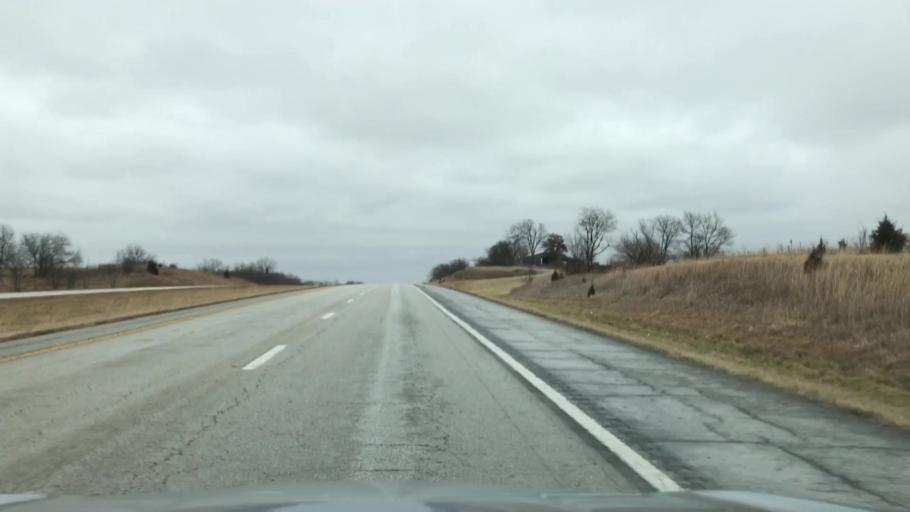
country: US
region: Missouri
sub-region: Caldwell County
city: Hamilton
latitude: 39.7501
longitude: -94.1088
